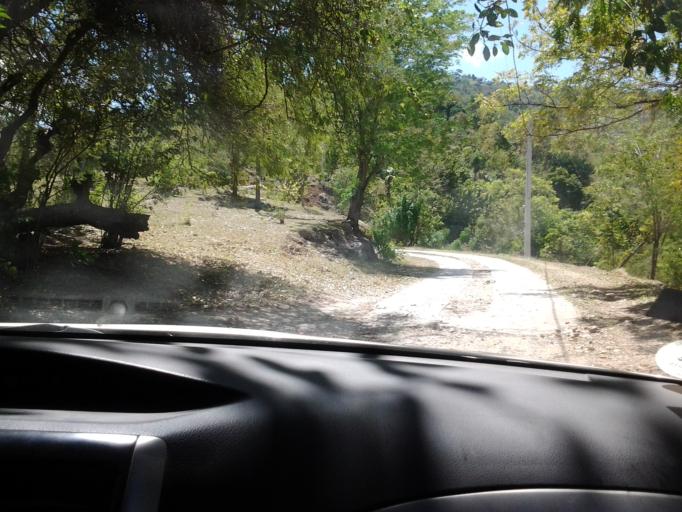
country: HT
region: Ouest
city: Grangwav
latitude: 18.4138
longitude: -72.8086
